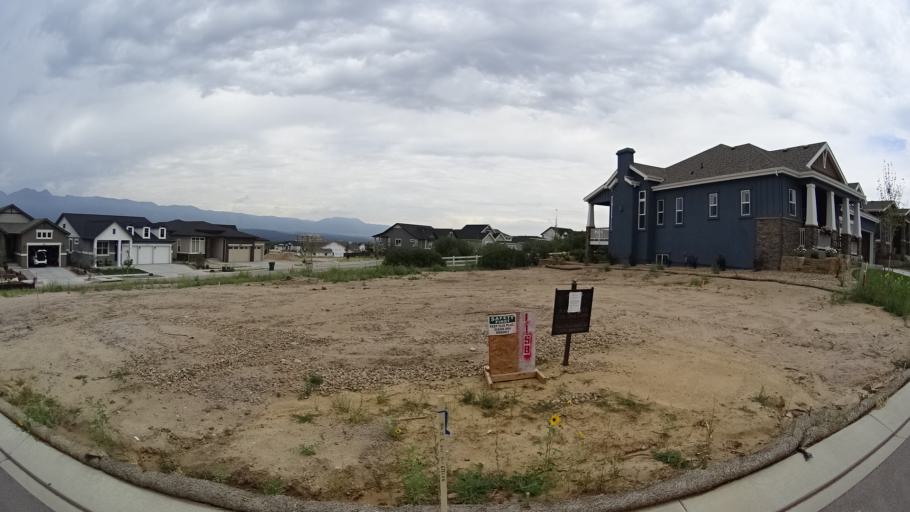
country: US
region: Colorado
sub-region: El Paso County
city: Gleneagle
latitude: 39.0046
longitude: -104.8075
